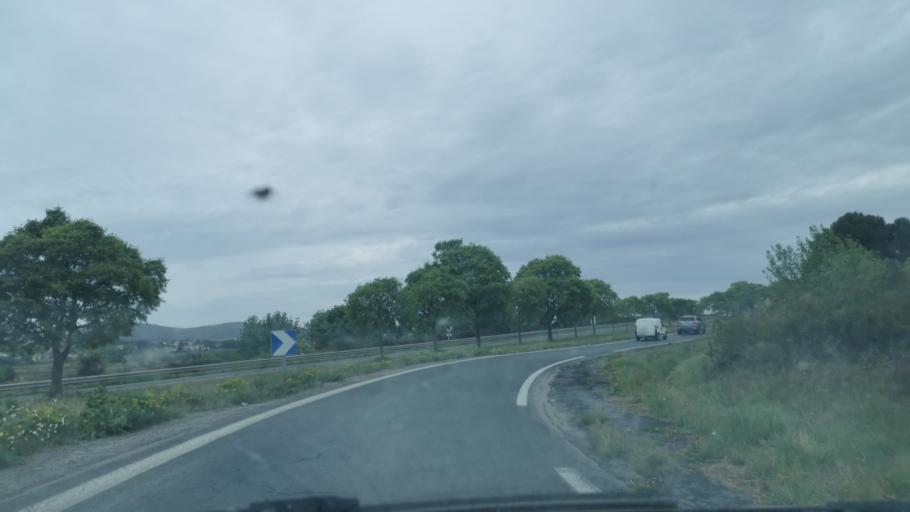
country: FR
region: Languedoc-Roussillon
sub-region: Departement de l'Herault
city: Balaruc-le-Vieux
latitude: 43.4733
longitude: 3.6853
